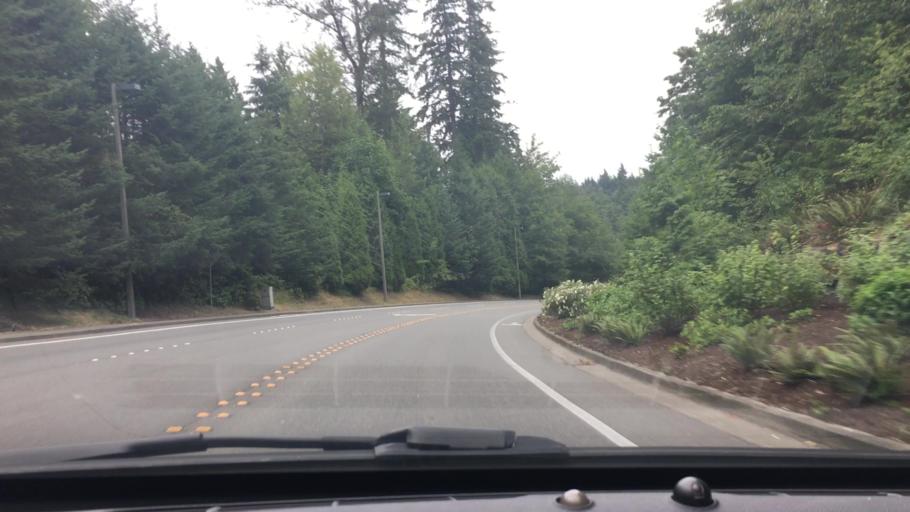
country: US
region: Washington
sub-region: King County
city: West Lake Sammamish
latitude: 47.5591
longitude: -122.1115
